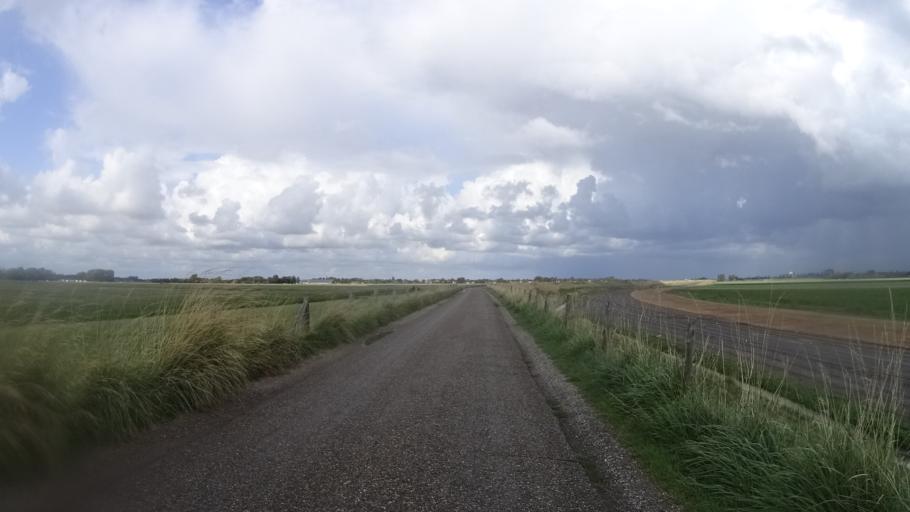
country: NL
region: North Holland
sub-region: Gemeente Schagen
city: Schagen
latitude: 52.7846
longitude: 4.7475
